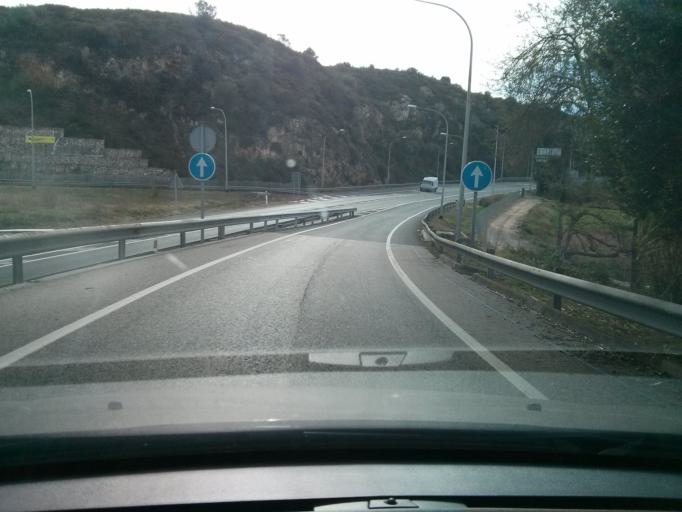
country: ES
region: Catalonia
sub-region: Provincia de Tarragona
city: Tarragona
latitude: 41.1405
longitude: 1.2390
